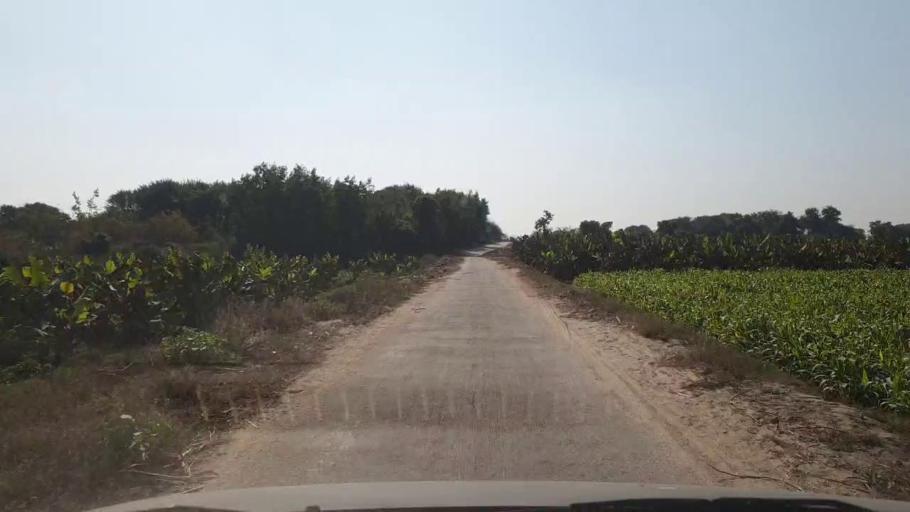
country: PK
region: Sindh
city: Tando Jam
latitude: 25.4215
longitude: 68.6320
